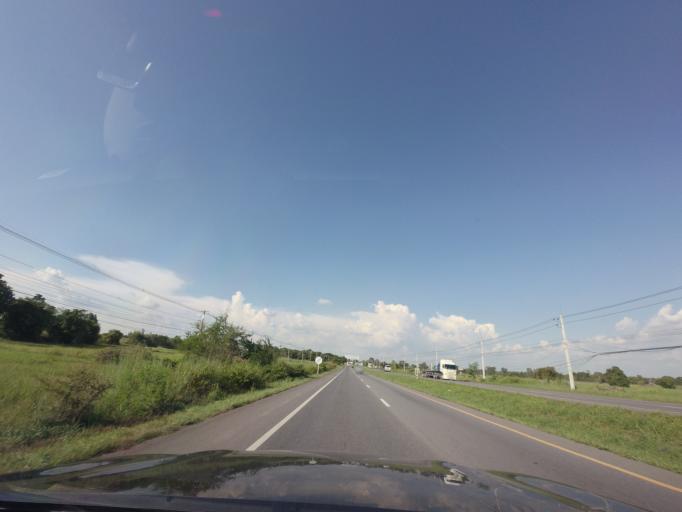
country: TH
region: Khon Kaen
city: Non Sila
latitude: 15.9537
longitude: 102.6850
